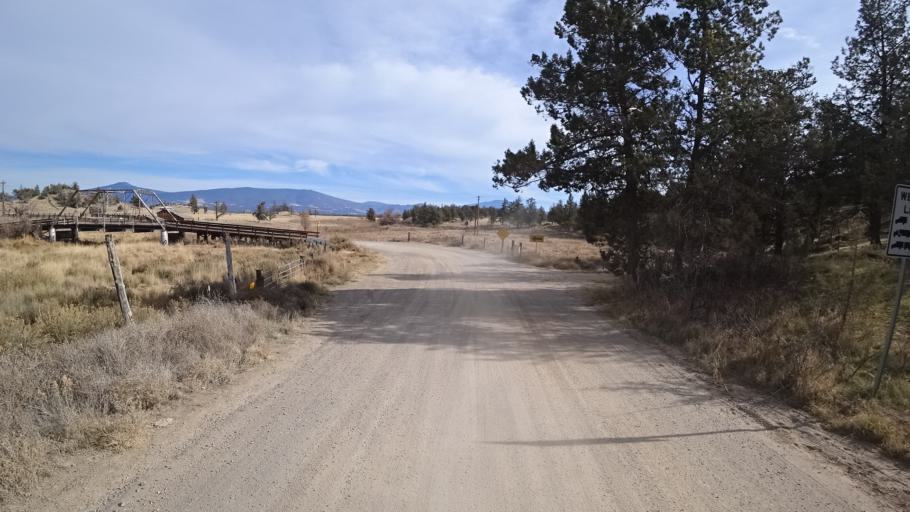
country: US
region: California
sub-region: Siskiyou County
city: Montague
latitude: 41.5902
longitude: -122.4388
